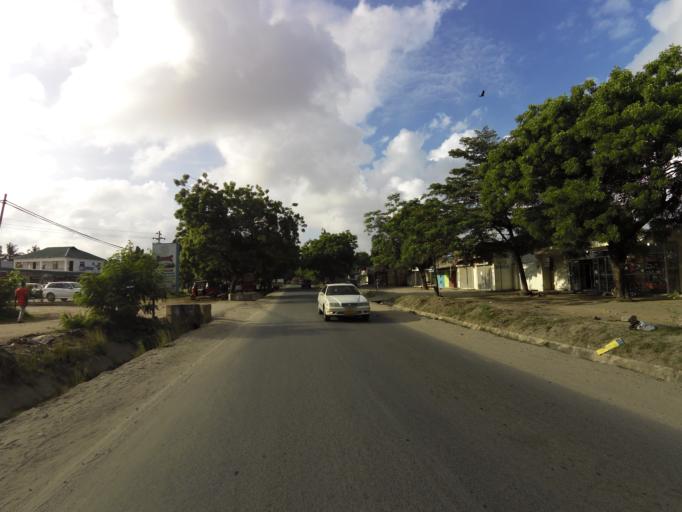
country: TZ
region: Dar es Salaam
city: Magomeni
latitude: -6.7759
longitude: 39.2416
